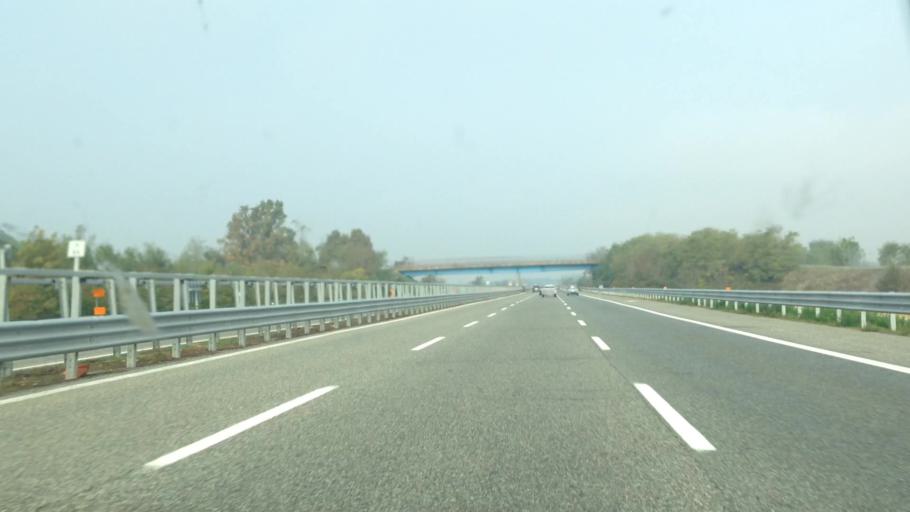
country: IT
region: Piedmont
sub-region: Provincia di Alessandria
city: Borgo San Martino
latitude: 45.0904
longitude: 8.5016
